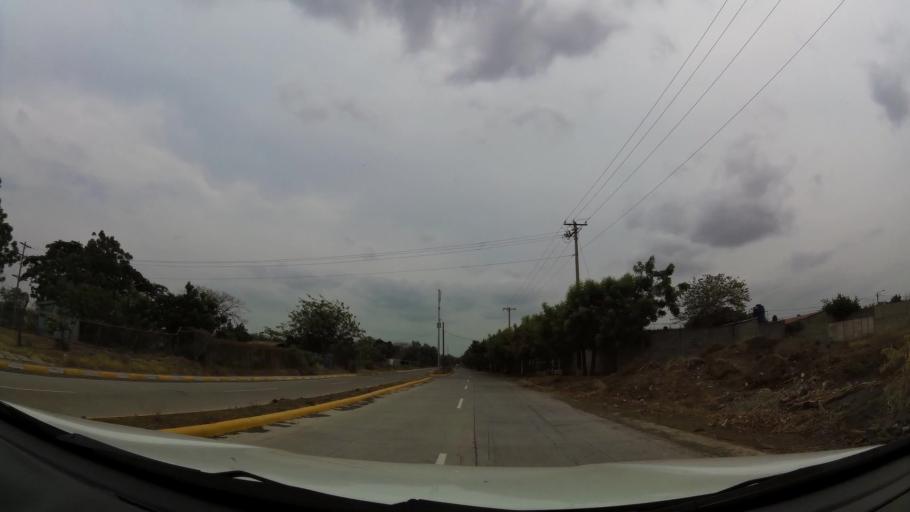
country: NI
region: Managua
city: Managua
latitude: 12.1166
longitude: -86.1714
